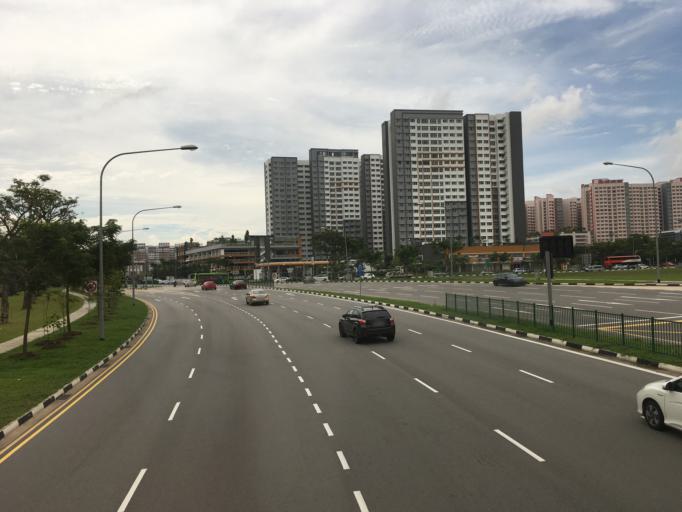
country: MY
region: Johor
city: Johor Bahru
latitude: 1.3484
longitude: 103.7382
